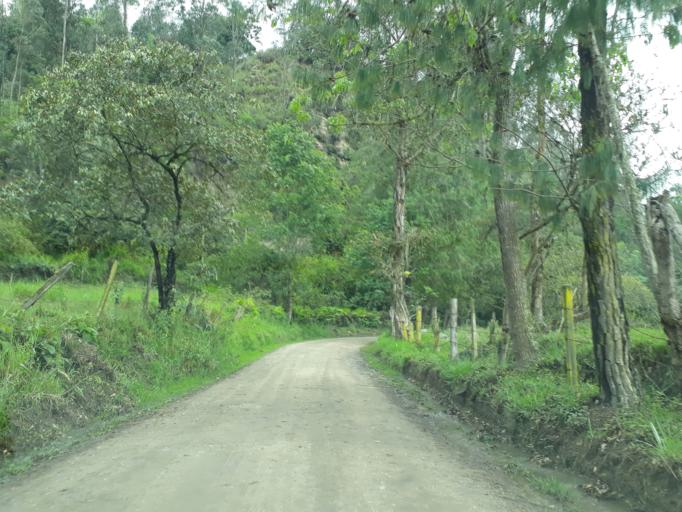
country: CO
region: Cundinamarca
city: Manta
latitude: 5.0019
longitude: -73.5495
